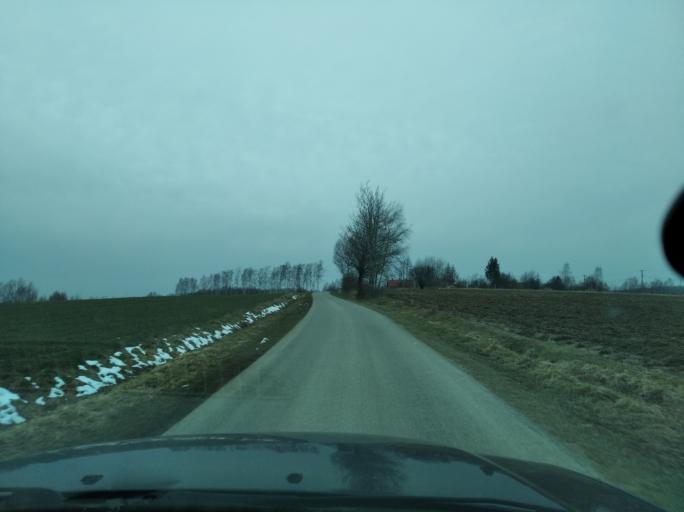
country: PL
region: Subcarpathian Voivodeship
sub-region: Powiat rzeszowski
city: Chmielnik
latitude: 49.9882
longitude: 22.1494
